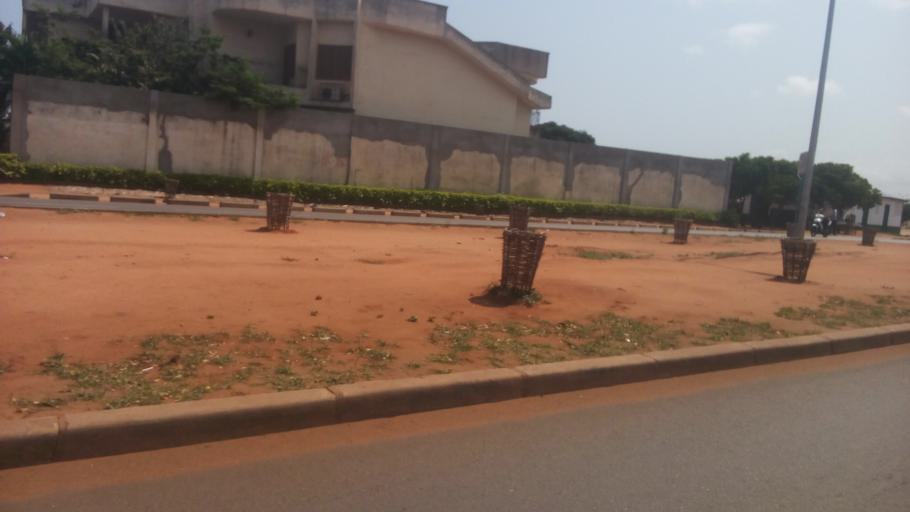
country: TG
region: Maritime
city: Lome
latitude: 6.1877
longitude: 1.2590
